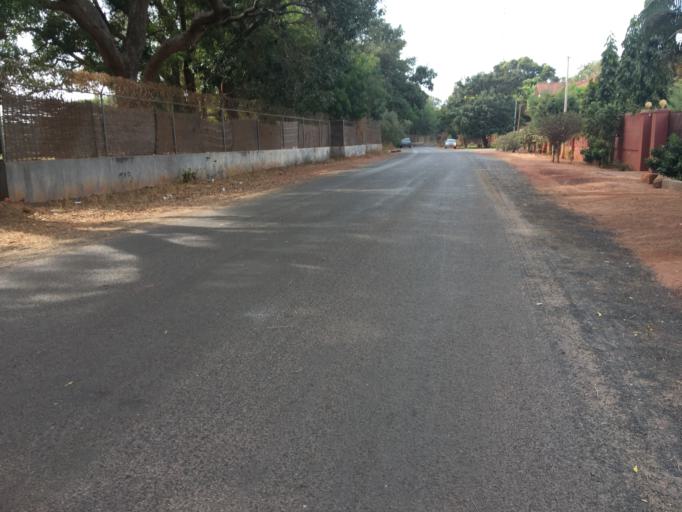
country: GM
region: Banjul
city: Bakau
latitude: 13.4738
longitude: -16.6851
